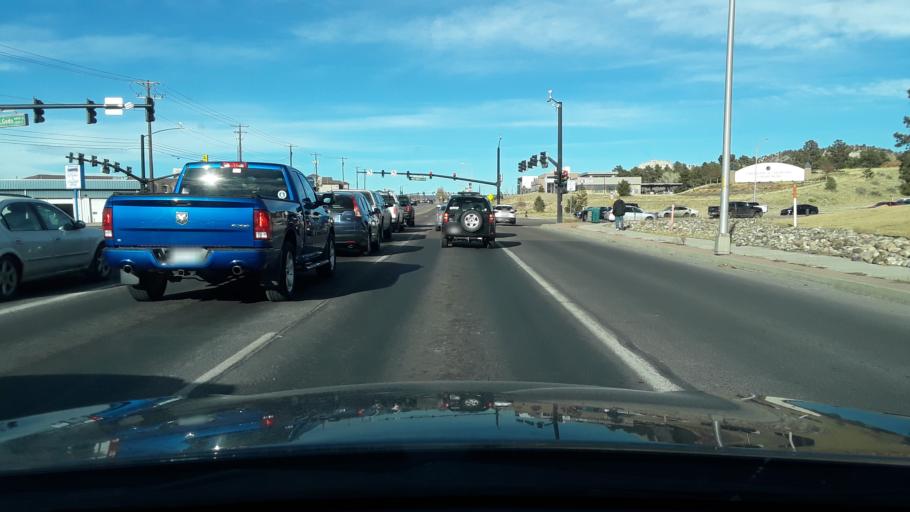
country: US
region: Colorado
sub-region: El Paso County
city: Colorado Springs
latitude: 38.8969
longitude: -104.8181
